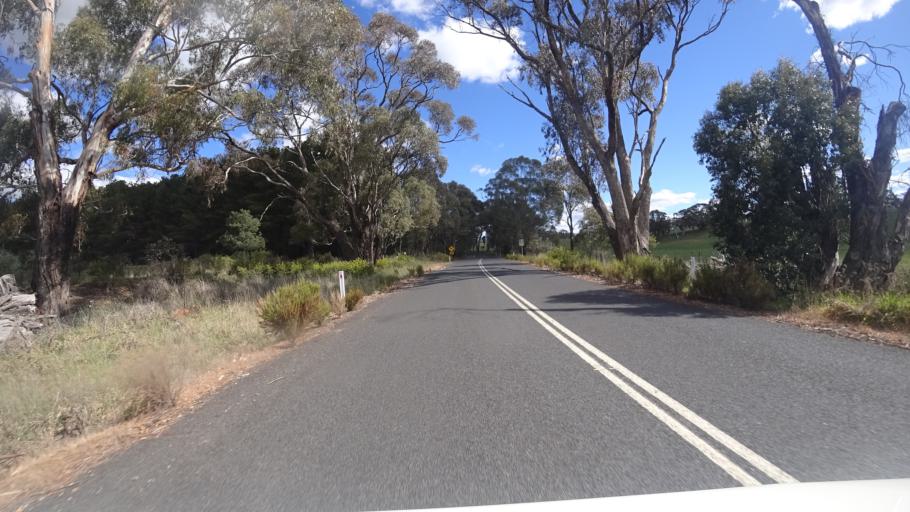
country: AU
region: New South Wales
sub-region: Oberon
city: Oberon
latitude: -33.6837
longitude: 149.7860
